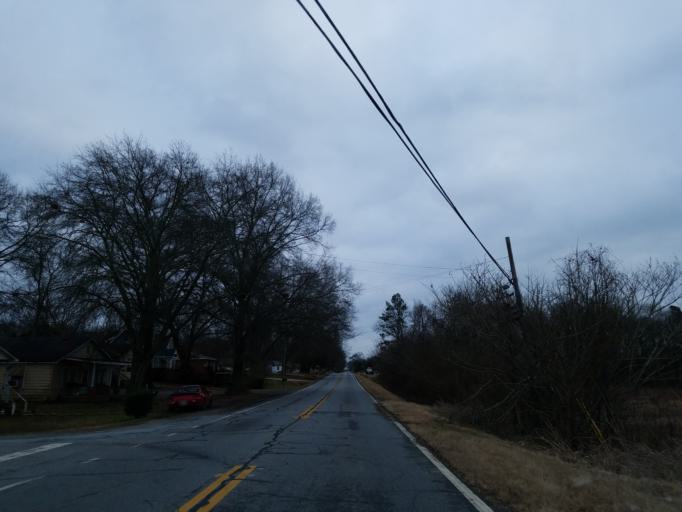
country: US
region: Georgia
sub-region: Bartow County
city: Cartersville
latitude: 34.2000
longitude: -84.8270
